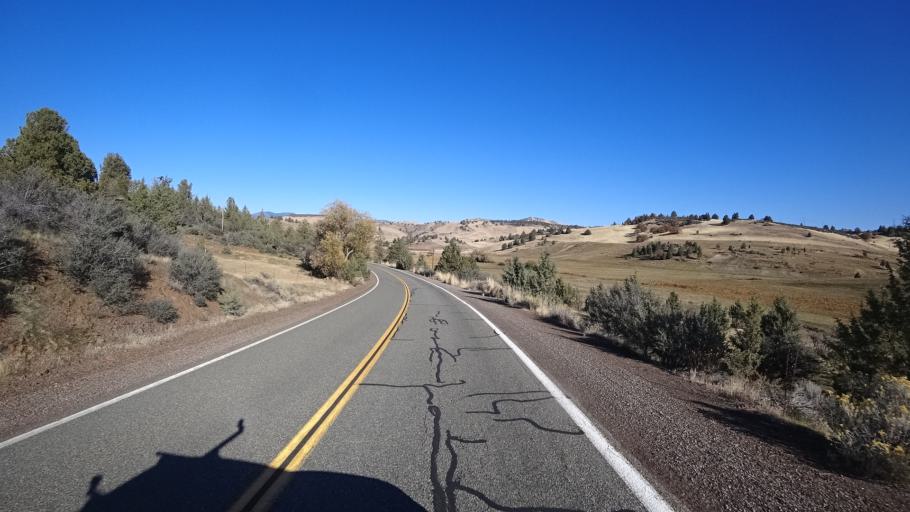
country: US
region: California
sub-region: Siskiyou County
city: Montague
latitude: 41.9131
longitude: -122.3719
